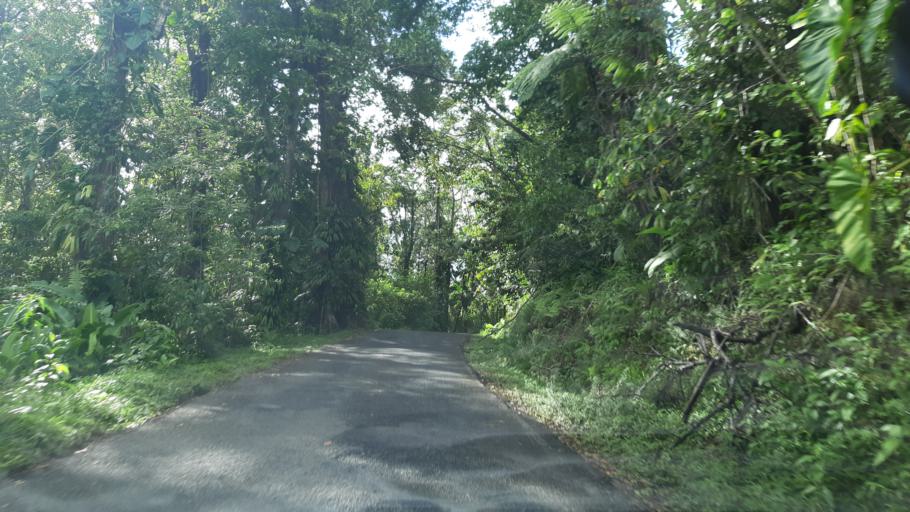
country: GP
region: Guadeloupe
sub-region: Guadeloupe
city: Saint-Claude
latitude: 16.0308
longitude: -61.6790
